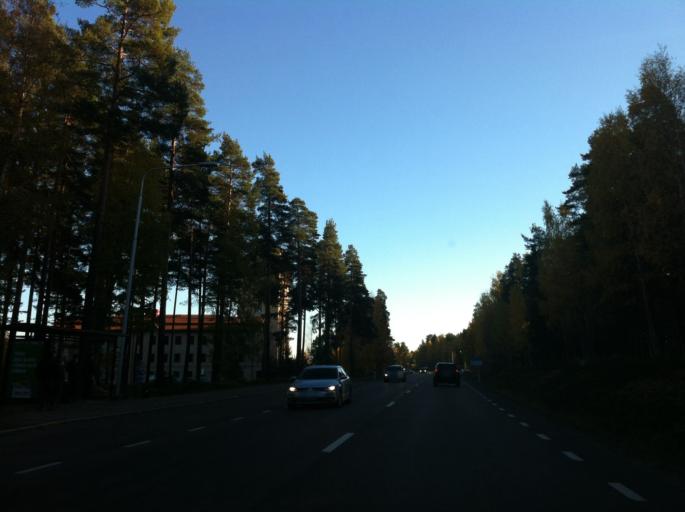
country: SE
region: Dalarna
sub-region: Faluns Kommun
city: Falun
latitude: 60.6156
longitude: 15.6500
